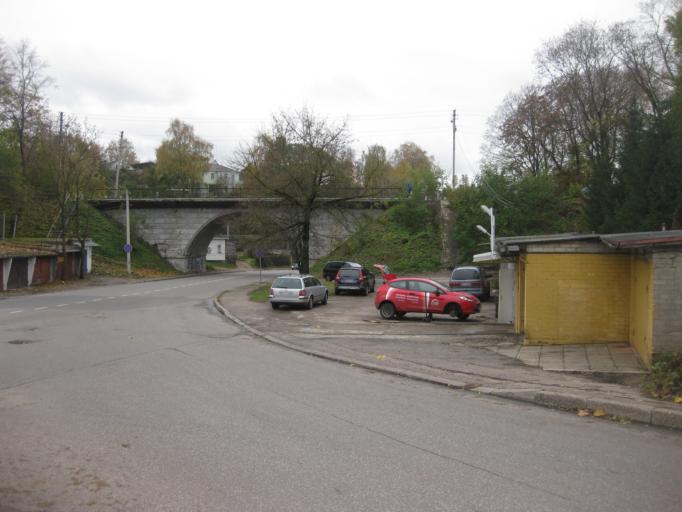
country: LT
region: Kauno apskritis
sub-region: Kaunas
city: Kaunas
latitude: 54.9057
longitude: 23.9147
